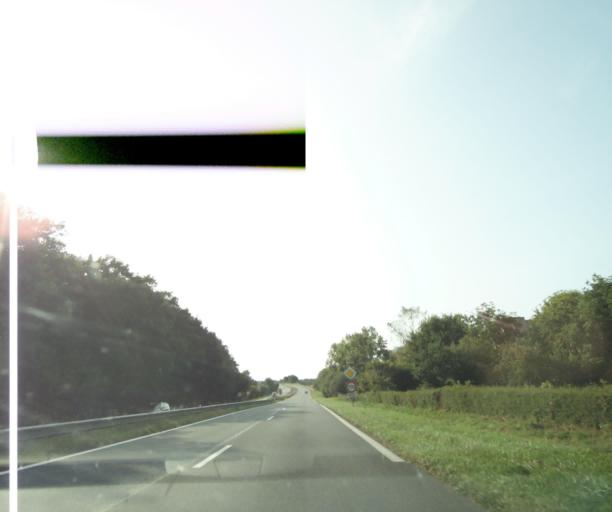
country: FR
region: Brittany
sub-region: Departement des Cotes-d'Armor
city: Jugon-les-Lacs
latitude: 48.4103
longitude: -2.3527
